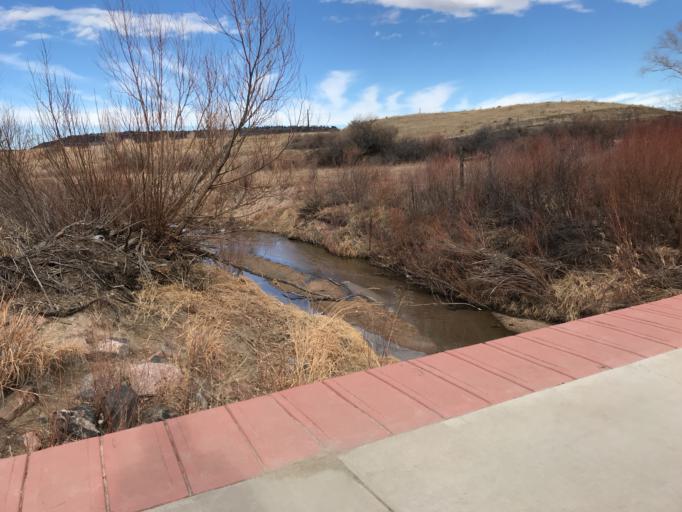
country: US
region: Colorado
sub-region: Douglas County
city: Castle Rock
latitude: 39.3962
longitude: -104.8712
